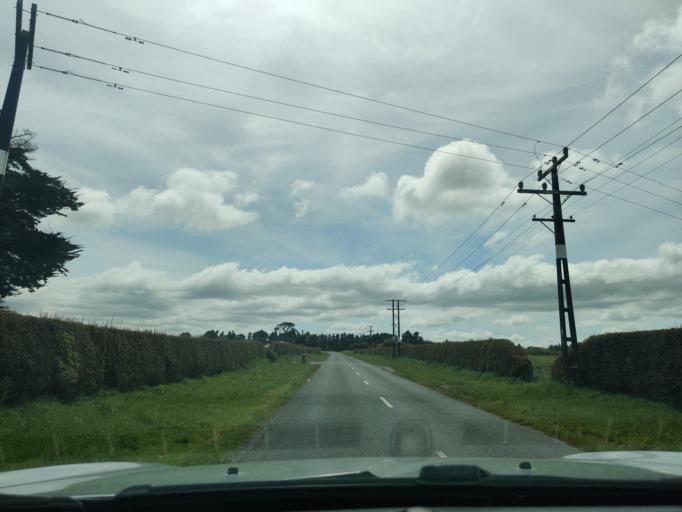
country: NZ
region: Taranaki
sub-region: South Taranaki District
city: Eltham
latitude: -39.3825
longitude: 174.1455
